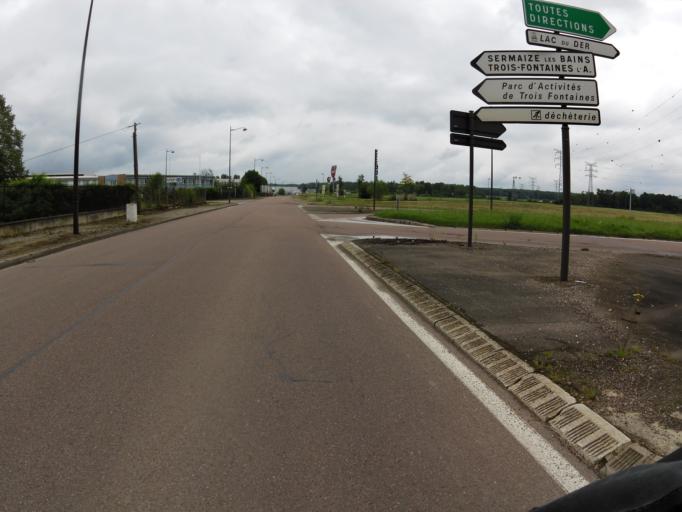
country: FR
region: Champagne-Ardenne
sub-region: Departement de la Haute-Marne
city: Saint-Dizier
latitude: 48.6486
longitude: 4.9346
